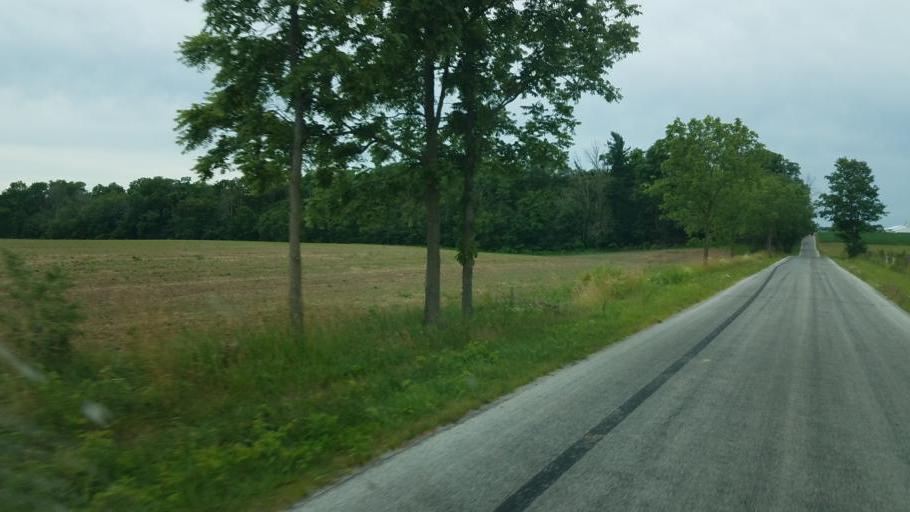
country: US
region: Ohio
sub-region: Huron County
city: Greenwich
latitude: 40.9260
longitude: -82.4553
